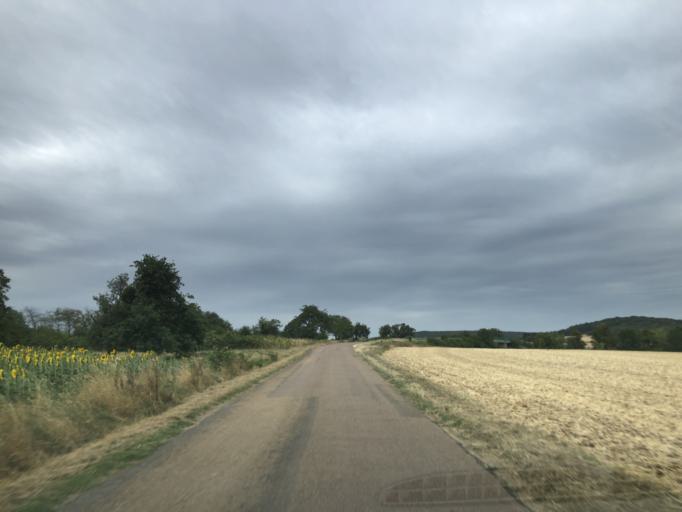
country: FR
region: Bourgogne
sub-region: Departement de l'Yonne
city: Aillant-sur-Tholon
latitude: 47.9090
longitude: 3.3429
